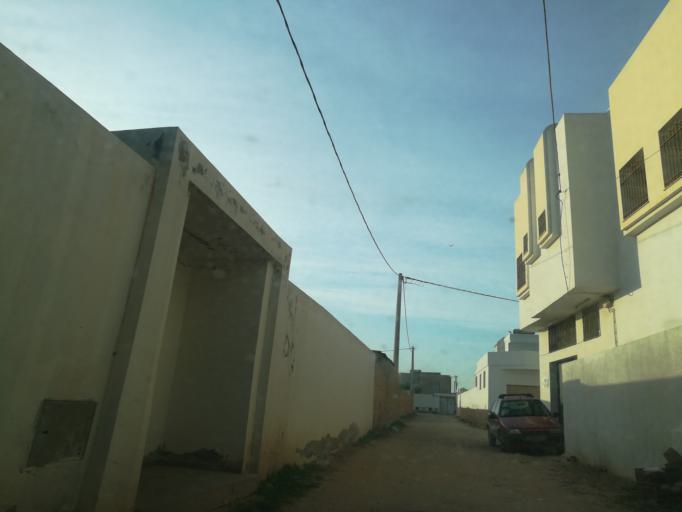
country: TN
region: Safaqis
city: Al Qarmadah
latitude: 34.8214
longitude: 10.7594
